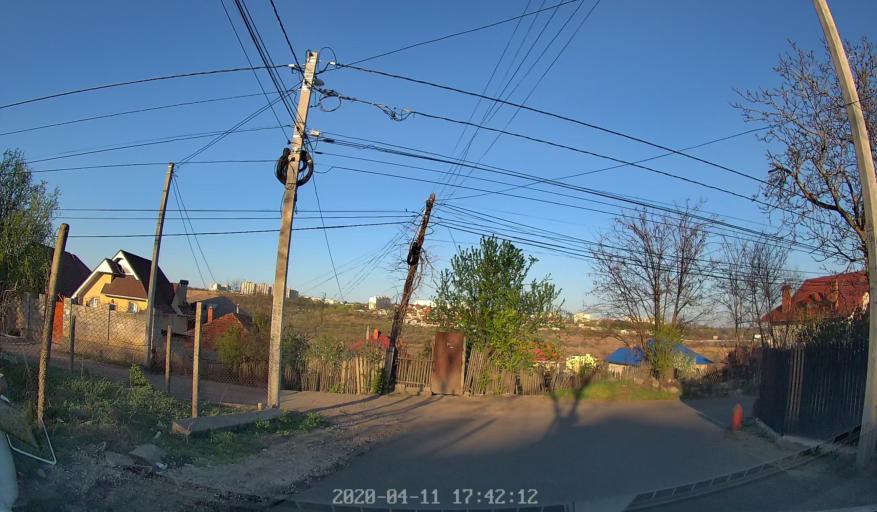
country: MD
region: Laloveni
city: Ialoveni
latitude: 46.9762
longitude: 28.8182
